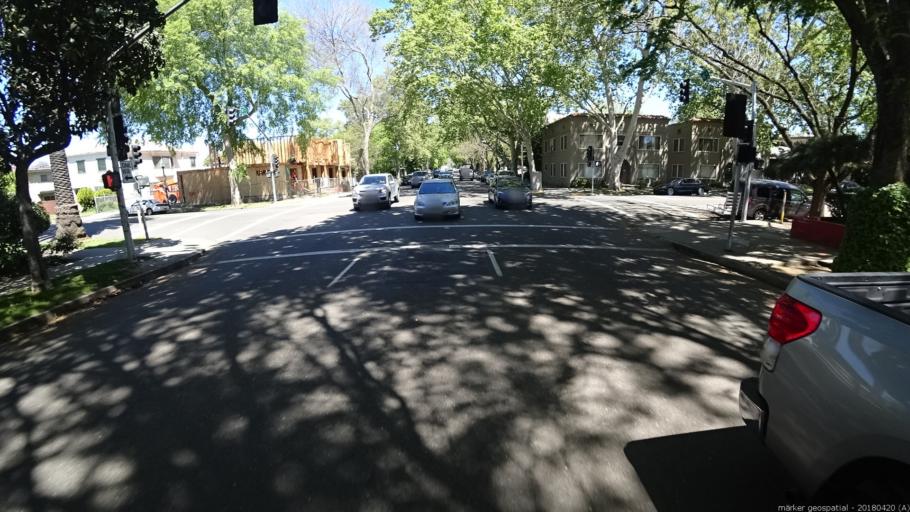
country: US
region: California
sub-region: Sacramento County
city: Sacramento
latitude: 38.5674
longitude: -121.4914
